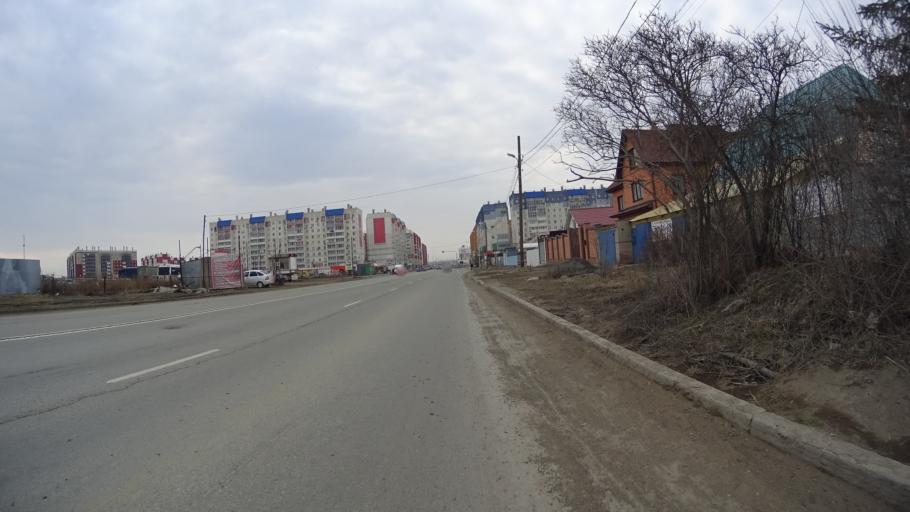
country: RU
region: Chelyabinsk
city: Zheleznodorozhnyy
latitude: 55.1649
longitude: 61.5224
